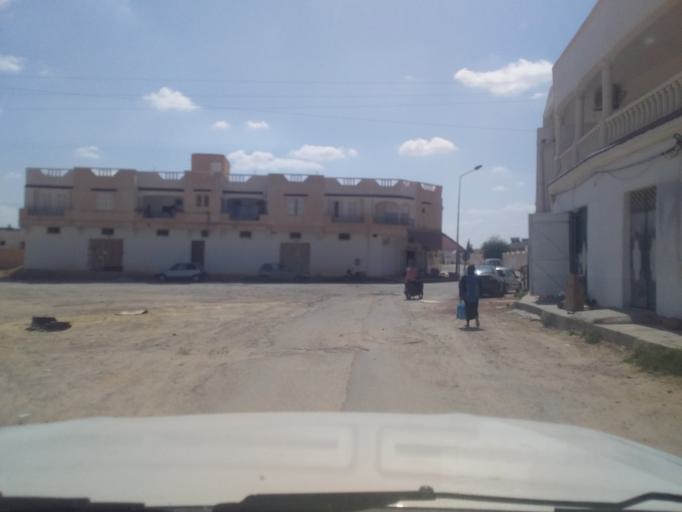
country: TN
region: Qabis
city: Matmata
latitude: 33.6146
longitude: 10.2937
